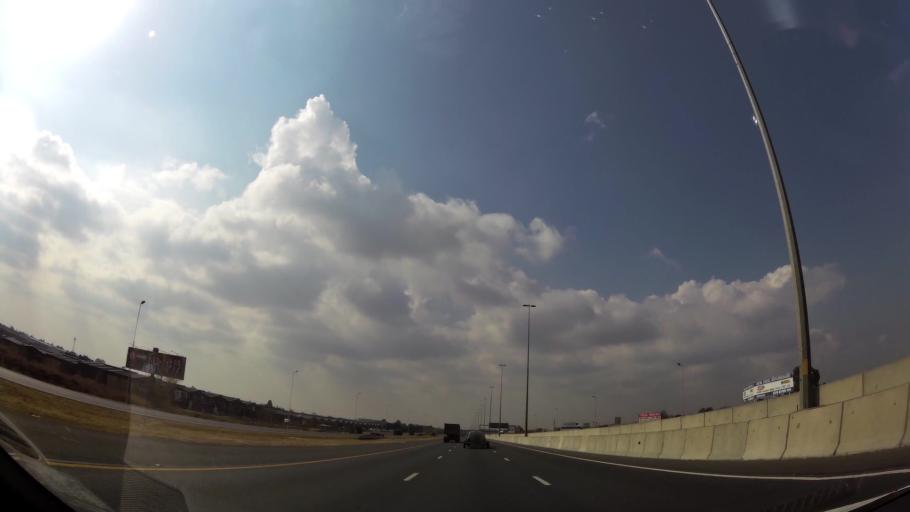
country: ZA
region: Gauteng
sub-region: Ekurhuleni Metropolitan Municipality
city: Boksburg
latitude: -26.1725
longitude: 28.2472
